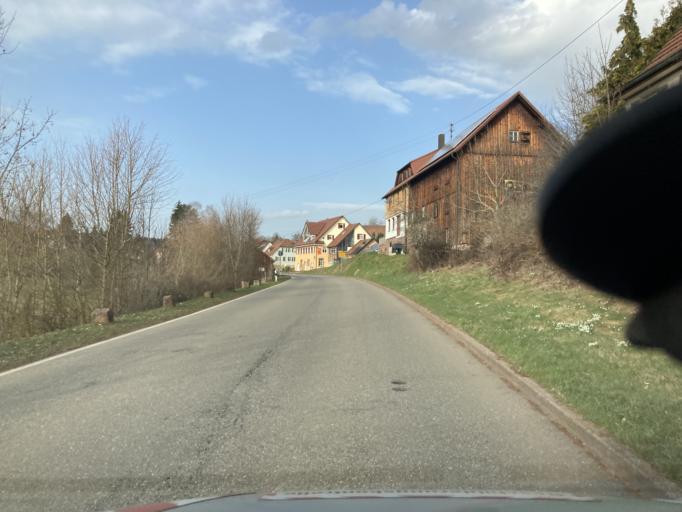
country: DE
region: Baden-Wuerttemberg
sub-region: Karlsruhe Region
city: Neuweiler
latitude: 48.6778
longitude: 8.6224
